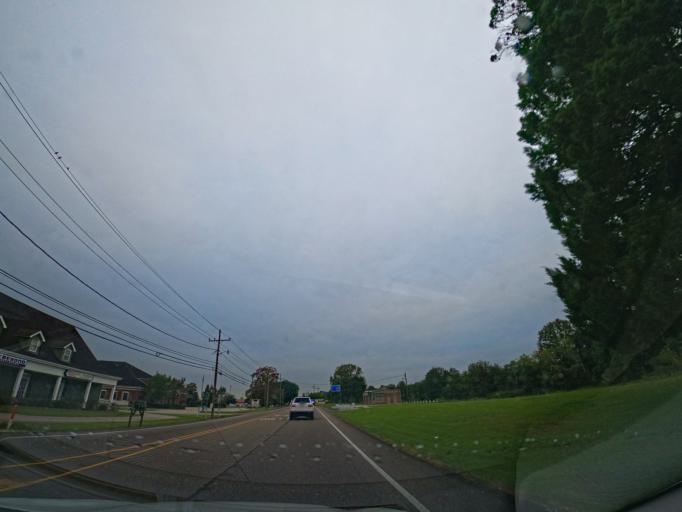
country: US
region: Louisiana
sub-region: Lafourche Parish
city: Mathews
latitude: 29.7026
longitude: -90.5629
